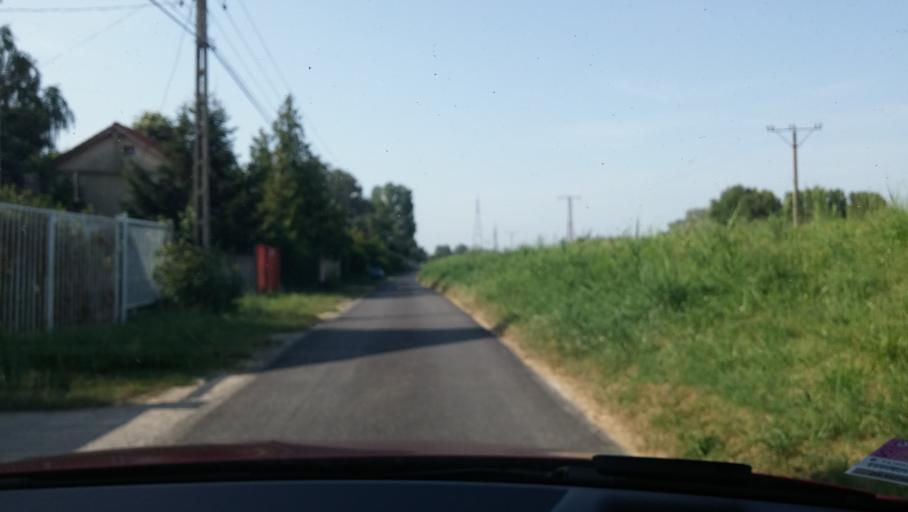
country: HU
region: Pest
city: Rackeve
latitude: 47.1848
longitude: 18.9480
